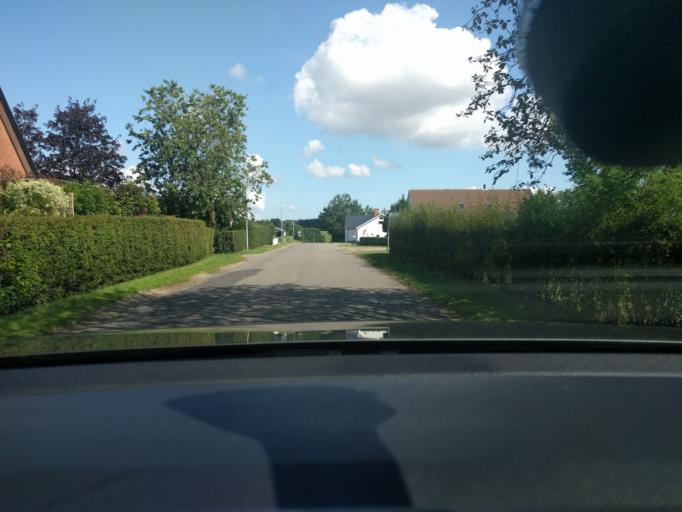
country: DK
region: Central Jutland
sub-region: Viborg Kommune
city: Viborg
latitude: 56.4485
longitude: 9.2883
